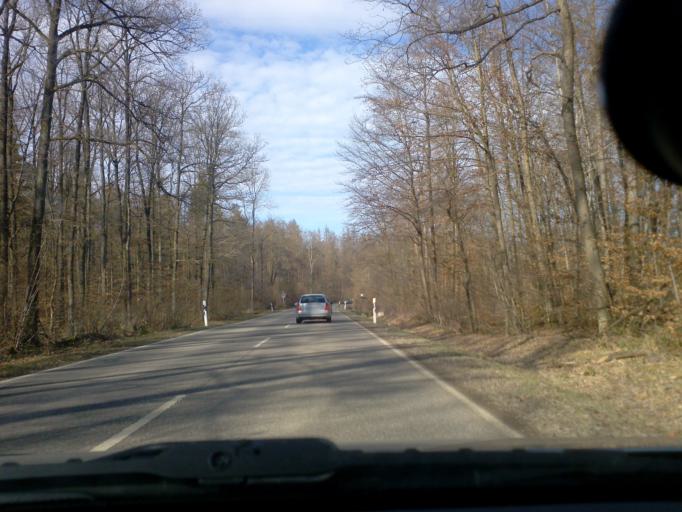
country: DE
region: Baden-Wuerttemberg
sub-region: Regierungsbezirk Stuttgart
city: Guglingen
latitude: 49.1094
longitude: 9.0152
